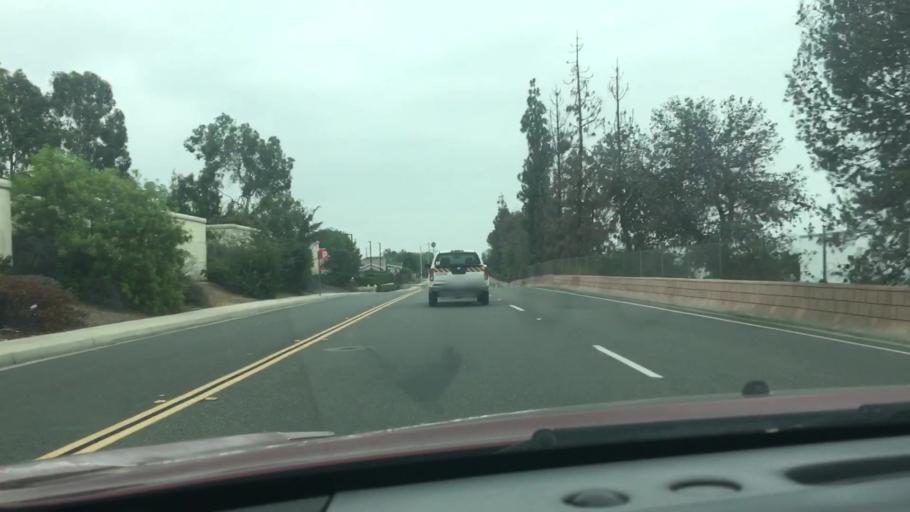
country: US
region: California
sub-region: Orange County
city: Buena Park
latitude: 33.8874
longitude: -118.0107
